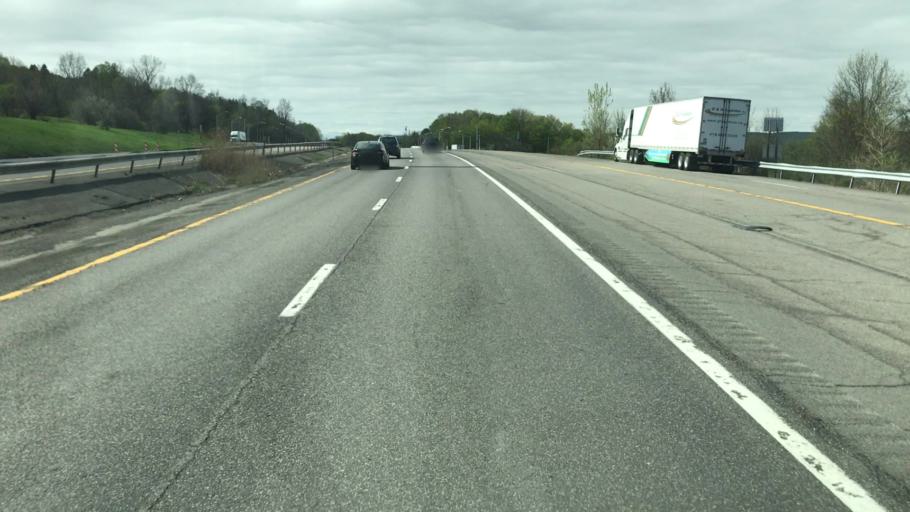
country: US
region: New York
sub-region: Onondaga County
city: Nedrow
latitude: 42.8605
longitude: -76.1174
